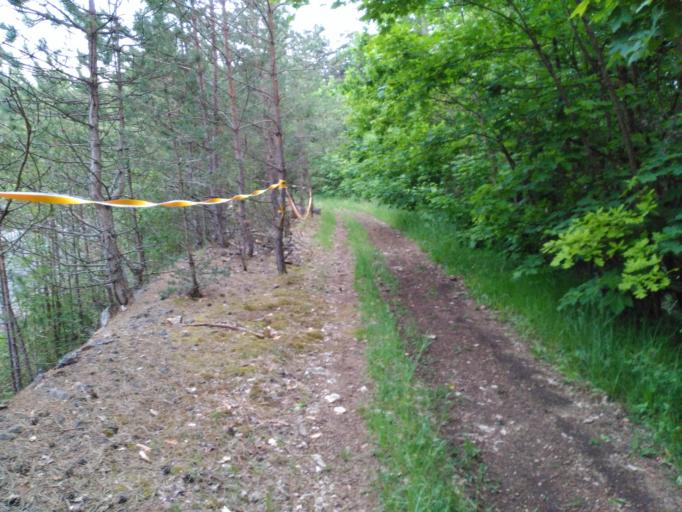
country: CZ
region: Central Bohemia
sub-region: Okres Beroun
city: Beroun
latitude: 49.9068
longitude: 14.0880
